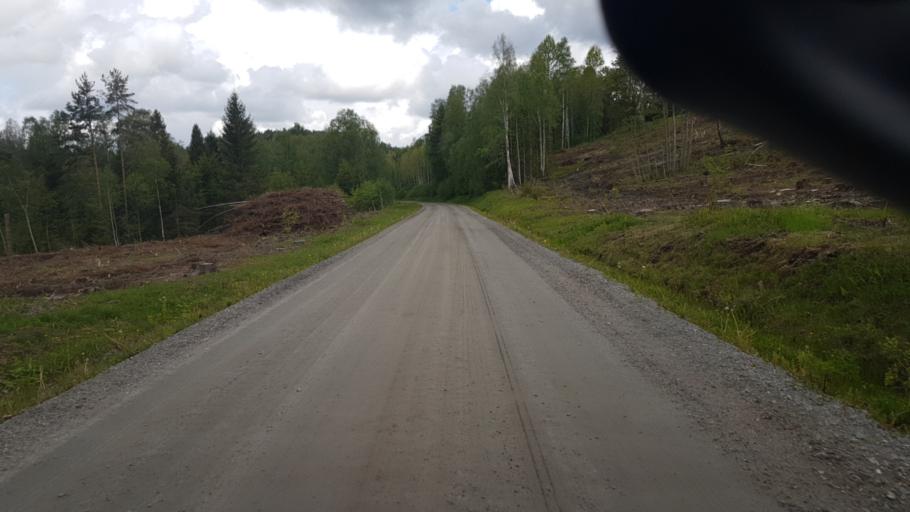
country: NO
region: Ostfold
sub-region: Romskog
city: Romskog
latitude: 59.6792
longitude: 11.9334
